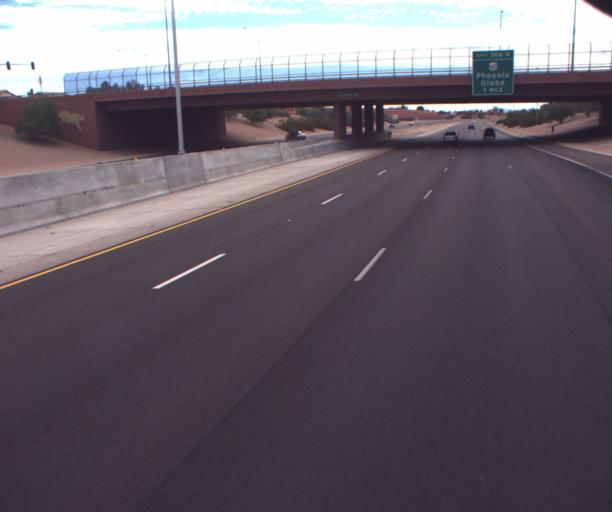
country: US
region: Arizona
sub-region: Pinal County
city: Apache Junction
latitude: 33.4087
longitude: -111.6405
